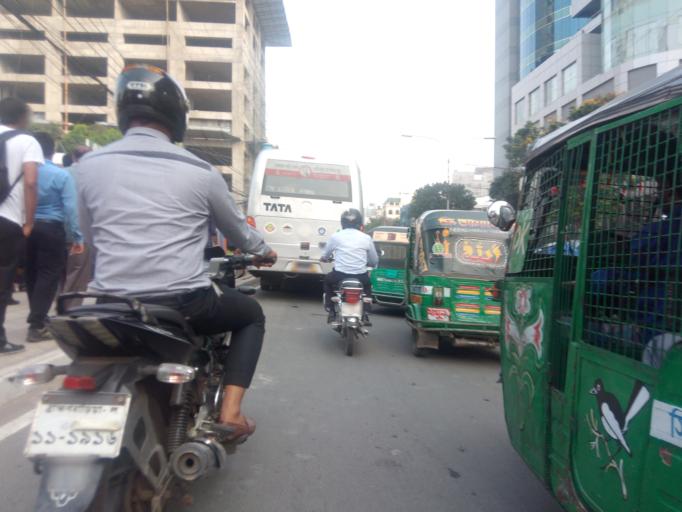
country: BD
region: Dhaka
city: Paltan
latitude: 23.7939
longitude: 90.4148
